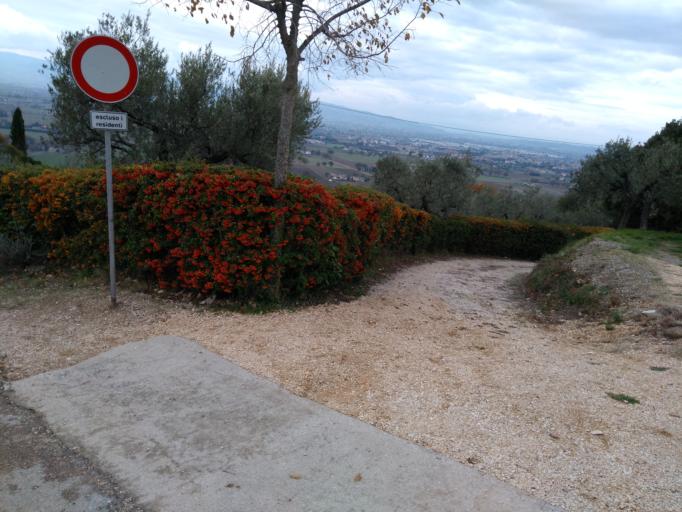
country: IT
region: Umbria
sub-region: Provincia di Perugia
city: Assisi
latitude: 43.0640
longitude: 12.6183
